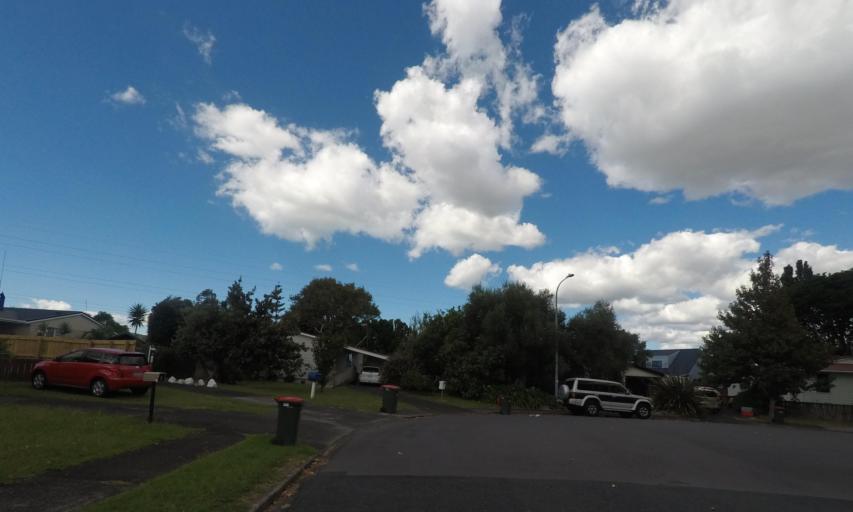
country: NZ
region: Auckland
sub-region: Auckland
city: Tamaki
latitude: -36.9189
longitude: 174.8676
